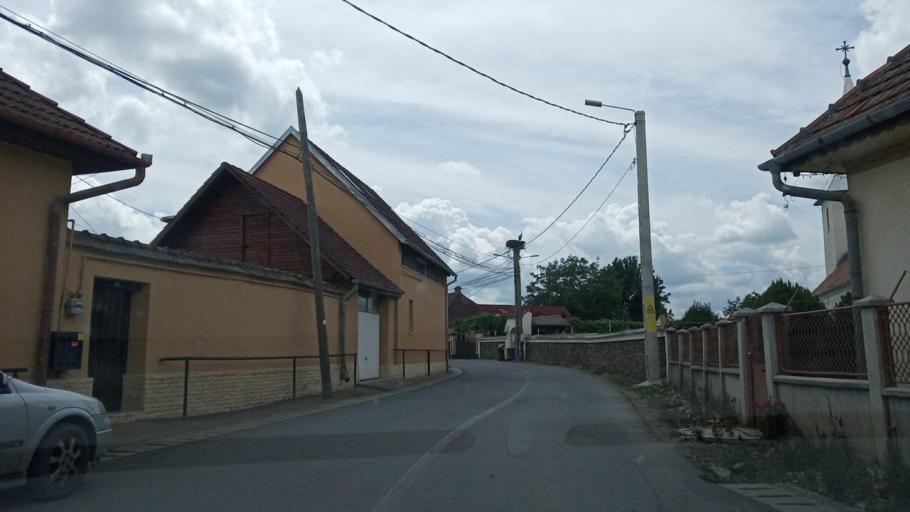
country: RO
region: Sibiu
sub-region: Comuna Cartisoara
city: Cartisoara
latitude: 45.7274
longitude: 24.5833
